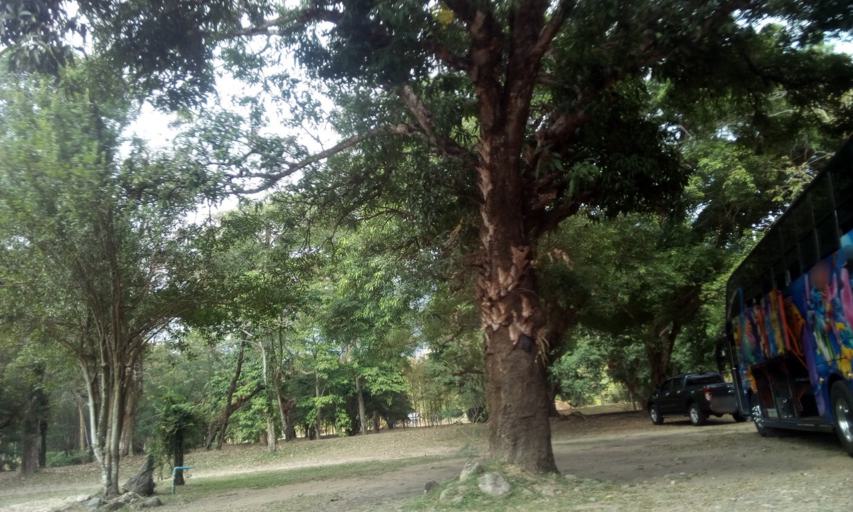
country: TH
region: Nakhon Nayok
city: Nakhon Nayok
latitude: 14.3249
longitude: 101.3048
